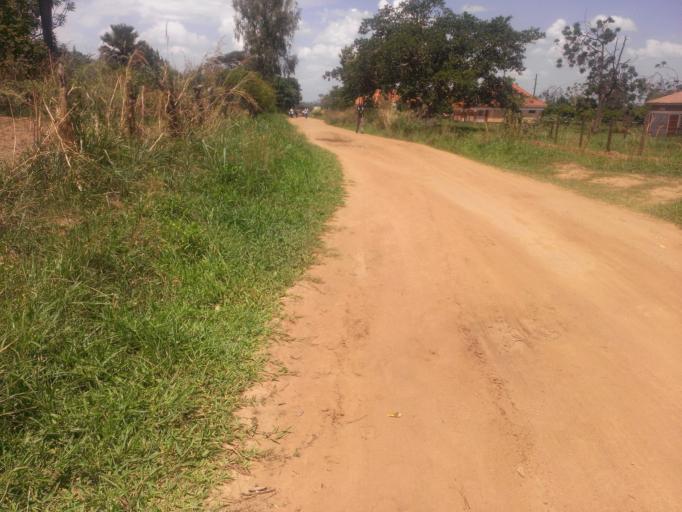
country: UG
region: Northern Region
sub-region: Gulu District
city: Gulu
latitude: 2.7847
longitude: 32.2963
